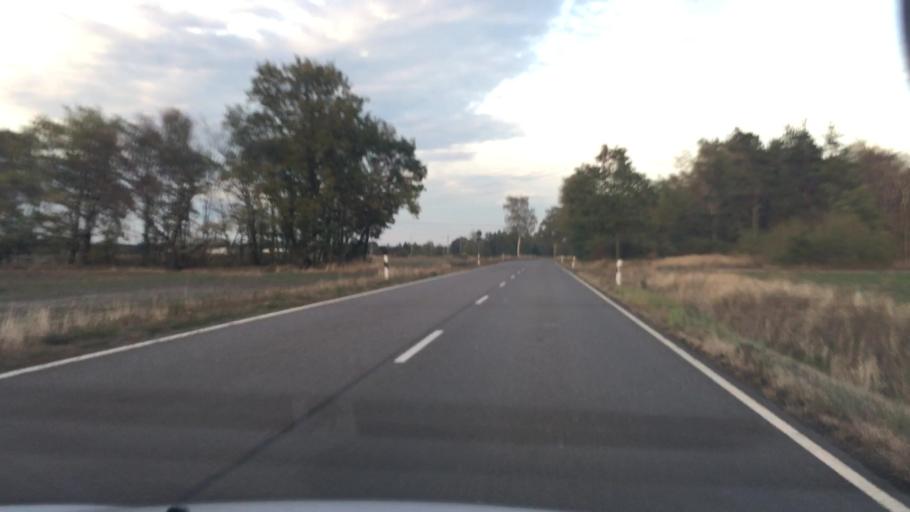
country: DE
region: Brandenburg
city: Grossraschen
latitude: 51.5729
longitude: 14.0816
